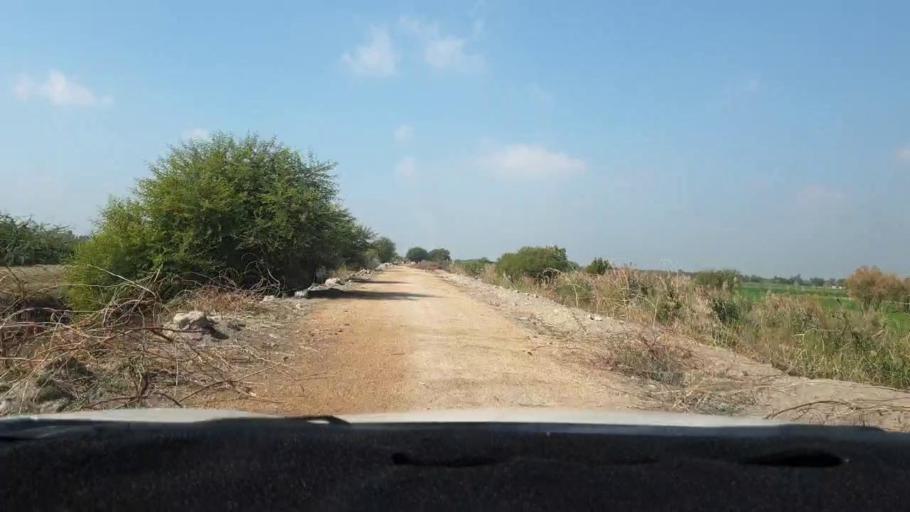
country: PK
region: Sindh
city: Berani
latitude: 25.7433
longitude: 68.9202
